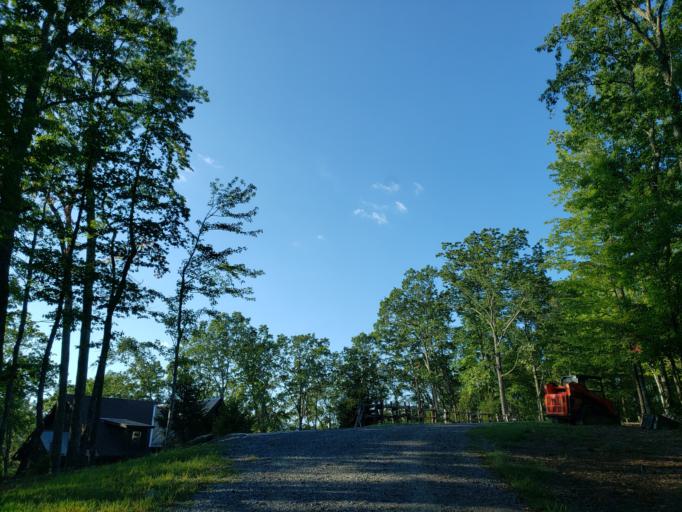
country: US
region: Georgia
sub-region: Fannin County
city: Blue Ridge
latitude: 34.6908
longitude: -84.2781
